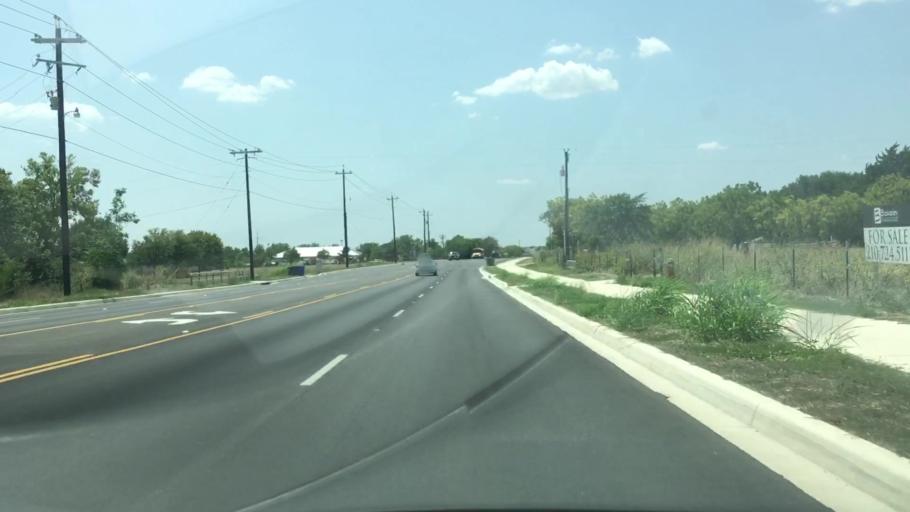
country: US
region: Texas
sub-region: Guadalupe County
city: Cibolo
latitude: 29.5697
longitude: -98.2431
